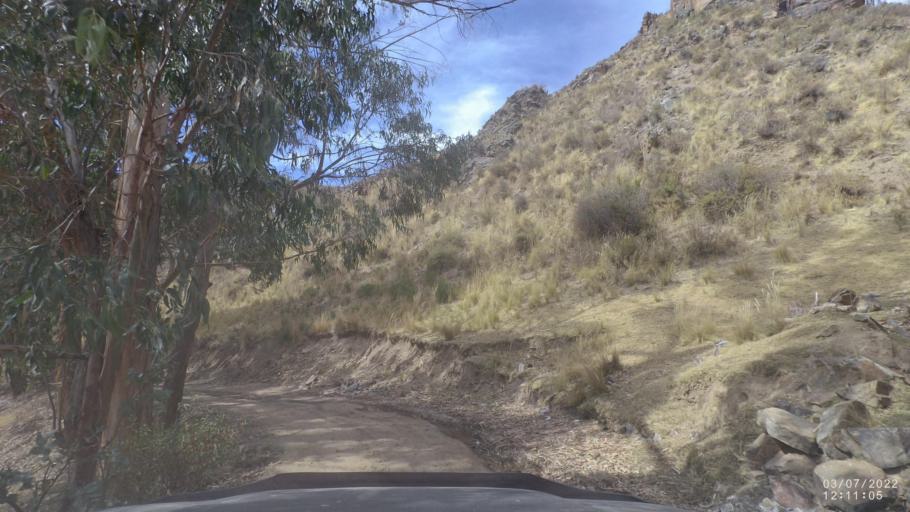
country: BO
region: Cochabamba
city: Irpa Irpa
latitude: -17.8412
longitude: -66.6153
